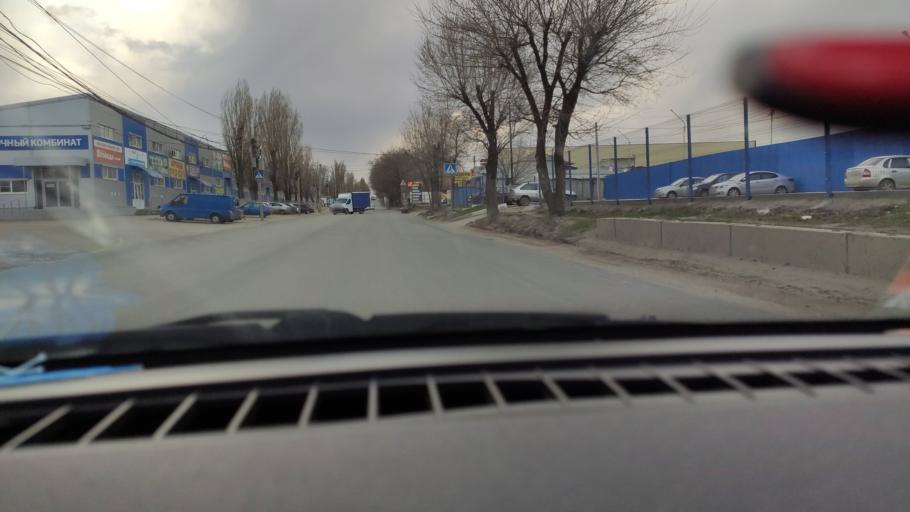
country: RU
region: Saratov
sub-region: Saratovskiy Rayon
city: Saratov
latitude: 51.6151
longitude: 45.9637
